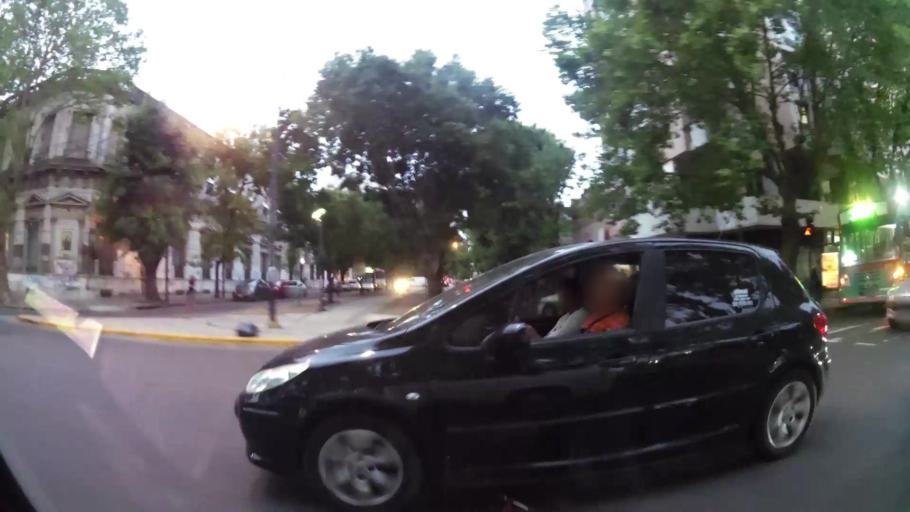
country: AR
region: Buenos Aires
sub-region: Partido de La Plata
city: La Plata
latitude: -34.9224
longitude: -57.9534
